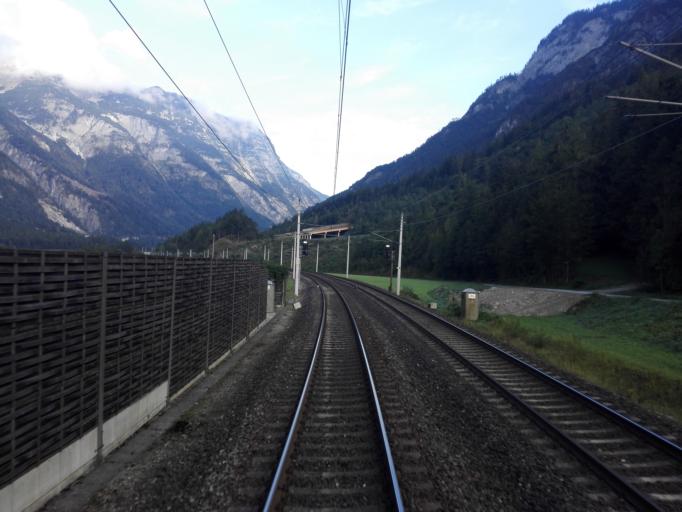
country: AT
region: Salzburg
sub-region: Politischer Bezirk Sankt Johann im Pongau
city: Werfen
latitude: 47.5012
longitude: 13.1773
